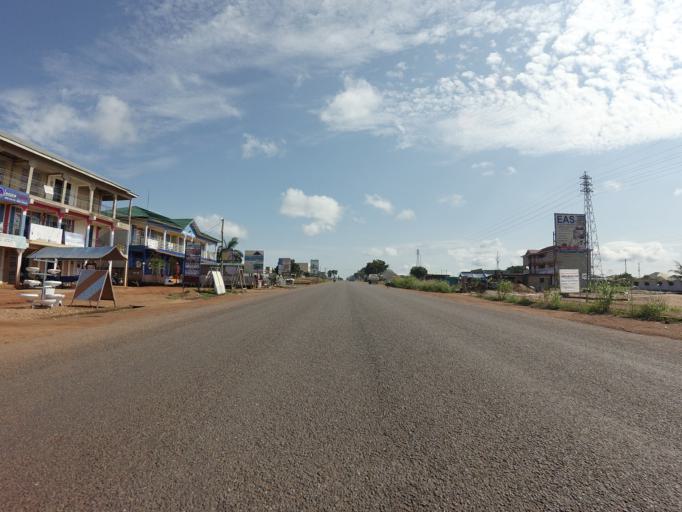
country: GH
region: Eastern
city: Aburi
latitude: 5.7905
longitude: -0.1302
